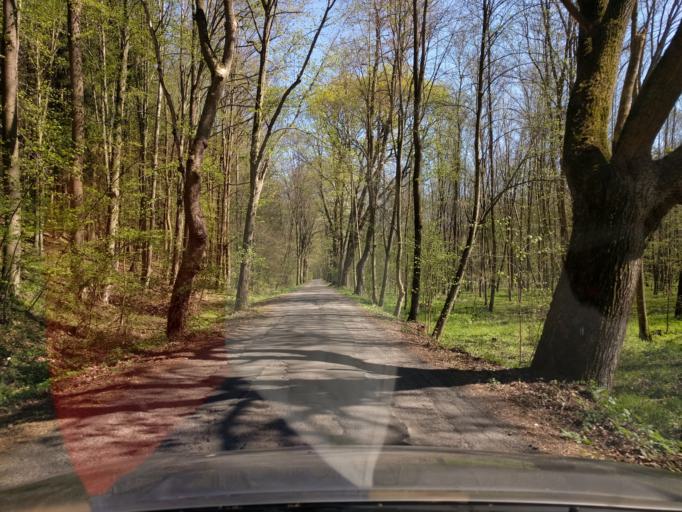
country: CZ
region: Central Bohemia
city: Cesky Brod
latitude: 50.0380
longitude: 14.8346
